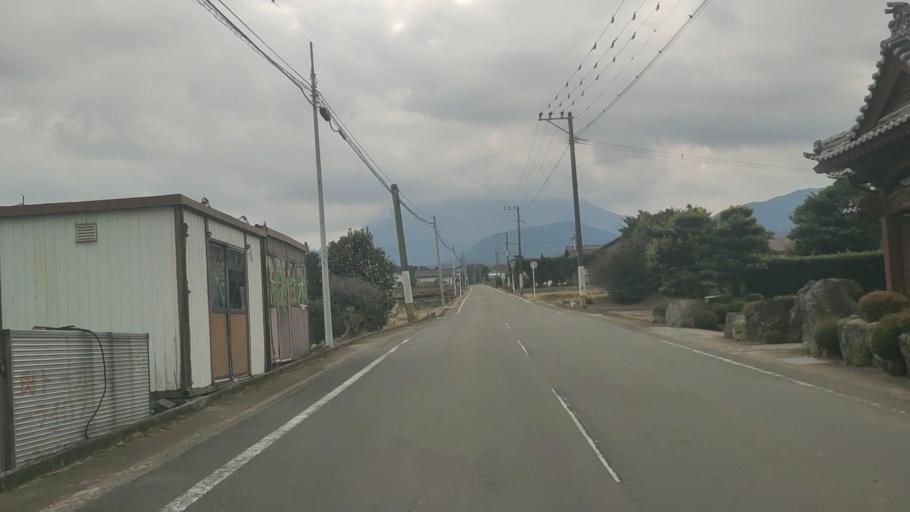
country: JP
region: Nagasaki
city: Shimabara
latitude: 32.8326
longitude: 130.2917
